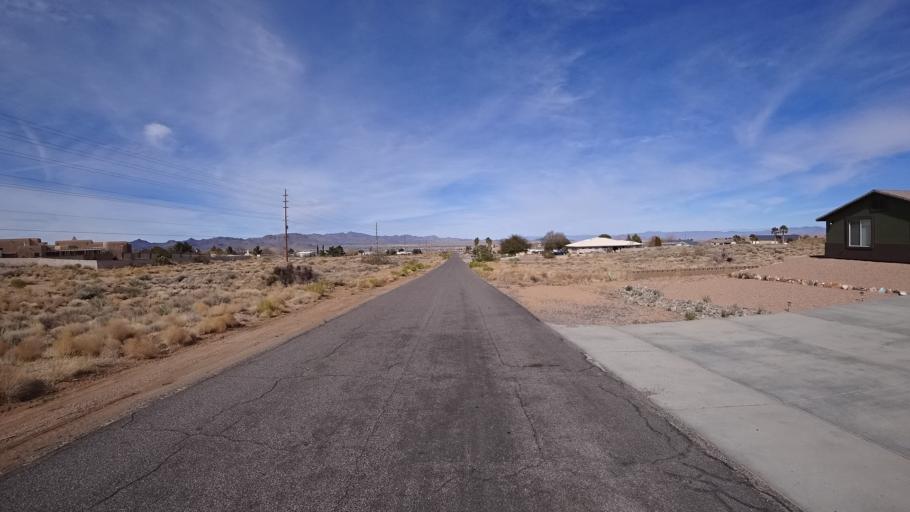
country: US
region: Arizona
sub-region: Mohave County
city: Kingman
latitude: 35.1907
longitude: -113.9852
